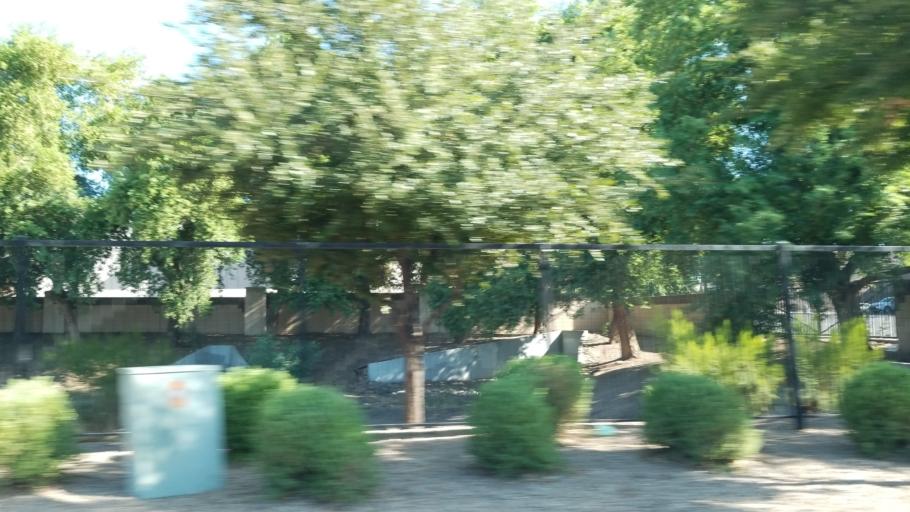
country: US
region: Arizona
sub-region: Maricopa County
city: Glendale
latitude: 33.5504
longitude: -112.1816
